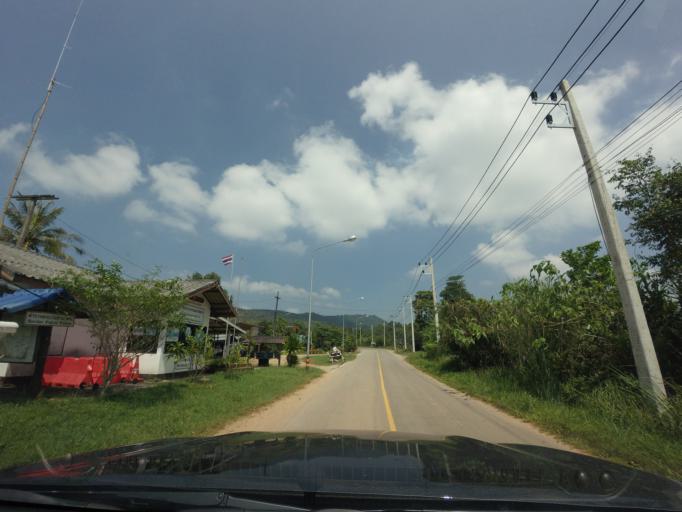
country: TH
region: Loei
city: Na Haeo
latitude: 17.4714
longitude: 100.9204
